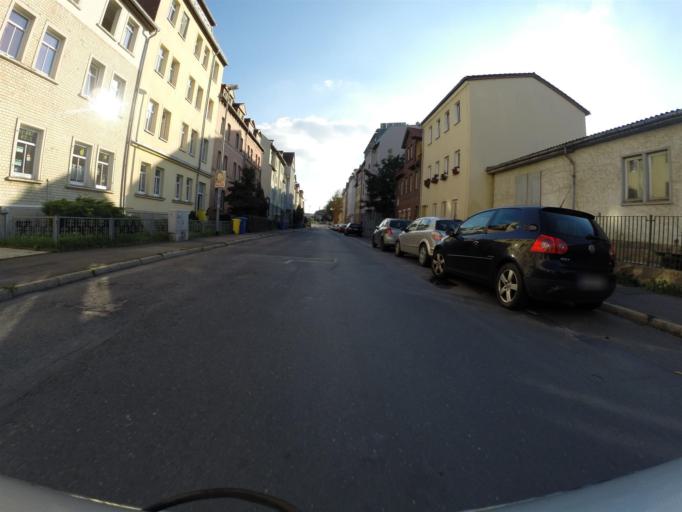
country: DE
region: Thuringia
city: Jena
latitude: 50.9365
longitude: 11.5943
